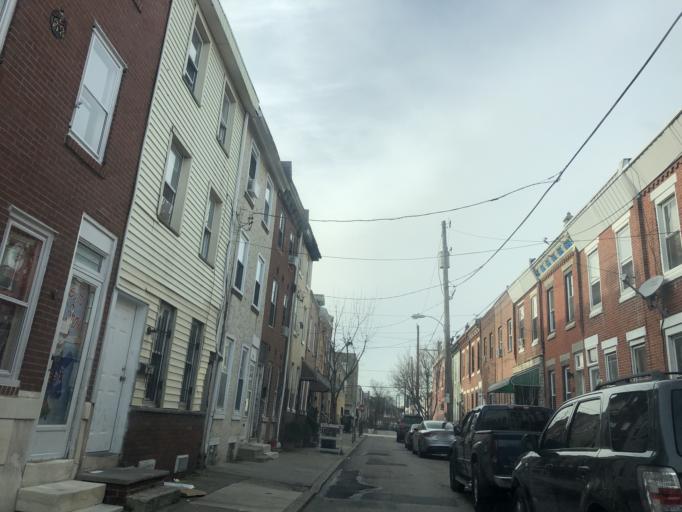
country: US
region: Pennsylvania
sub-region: Philadelphia County
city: Philadelphia
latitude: 39.9278
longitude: -75.1547
